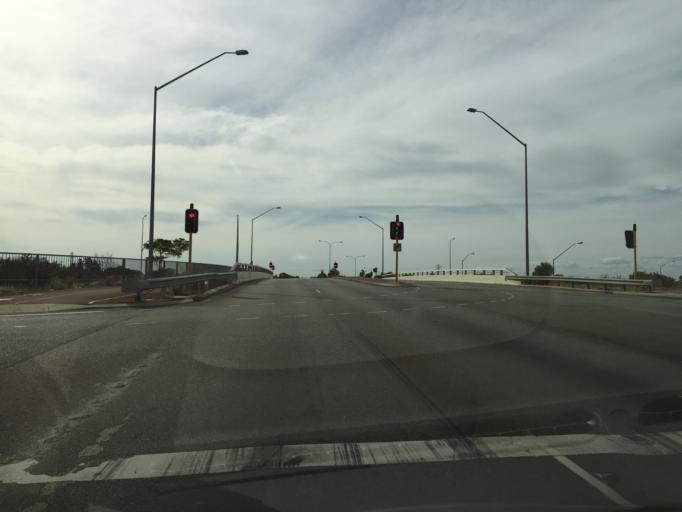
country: AU
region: Western Australia
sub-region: Canning
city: Canning Vale
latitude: -32.0578
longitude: 115.9051
